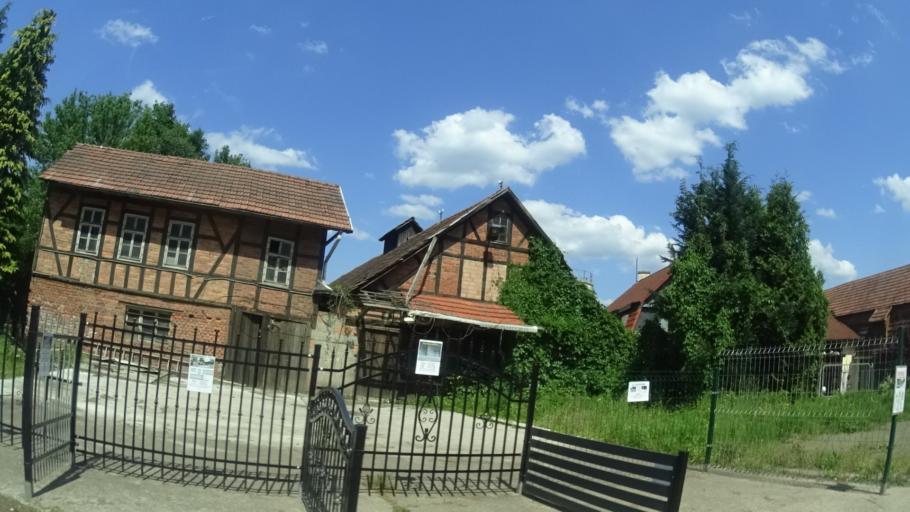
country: DE
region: Thuringia
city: Pappenheim
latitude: 50.7555
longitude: 10.4734
